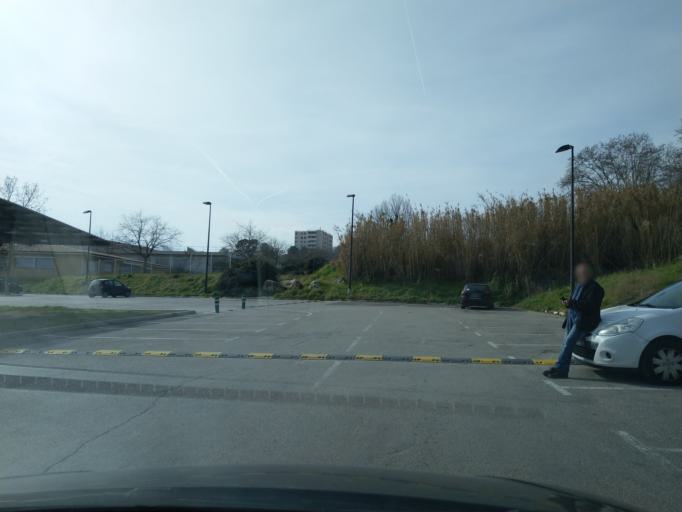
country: FR
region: Provence-Alpes-Cote d'Azur
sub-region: Departement des Bouches-du-Rhone
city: Marseille 12
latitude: 43.2961
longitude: 5.4420
